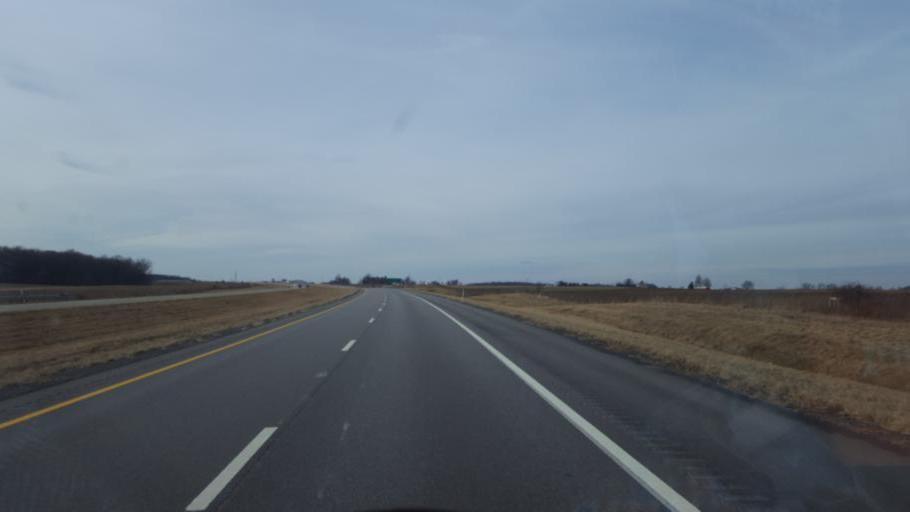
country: US
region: Ohio
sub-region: Wayne County
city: Apple Creek
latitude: 40.8071
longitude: -81.8272
